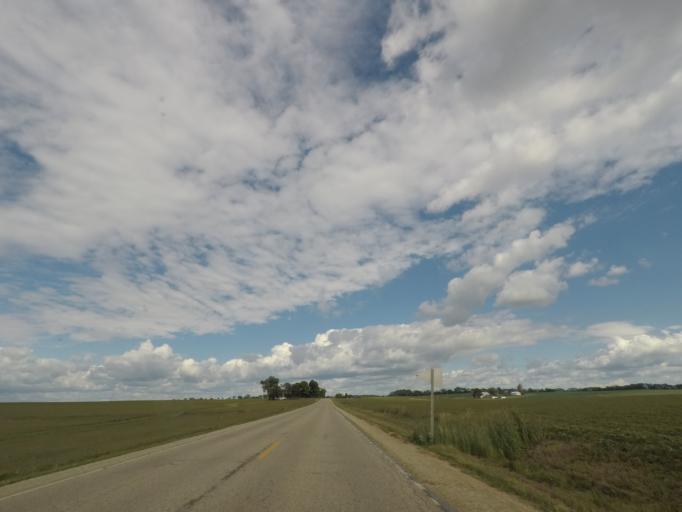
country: US
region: Wisconsin
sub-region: Rock County
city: Orfordville
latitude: 42.7046
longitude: -89.1570
